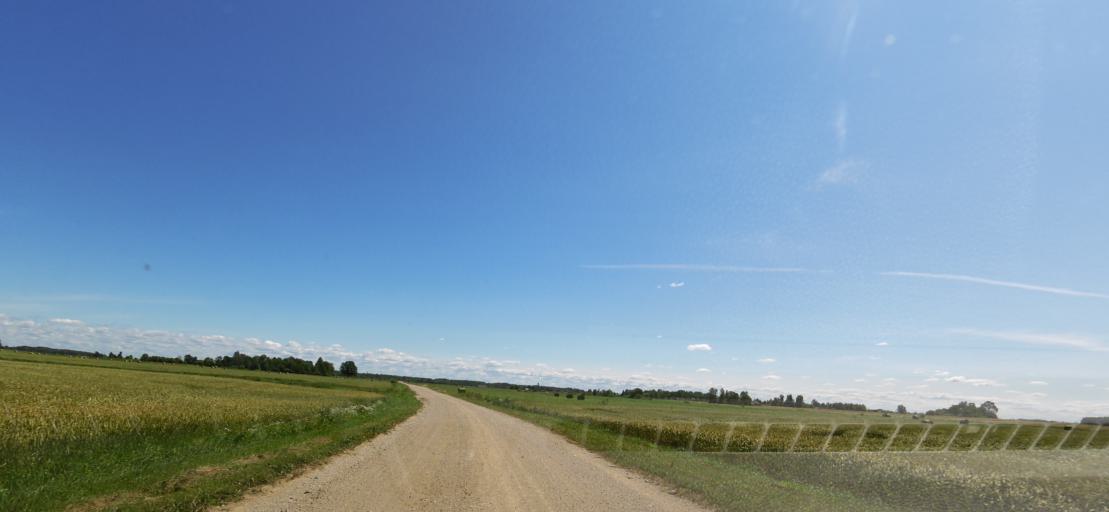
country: LT
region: Panevezys
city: Pasvalys
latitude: 56.2605
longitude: 24.5229
